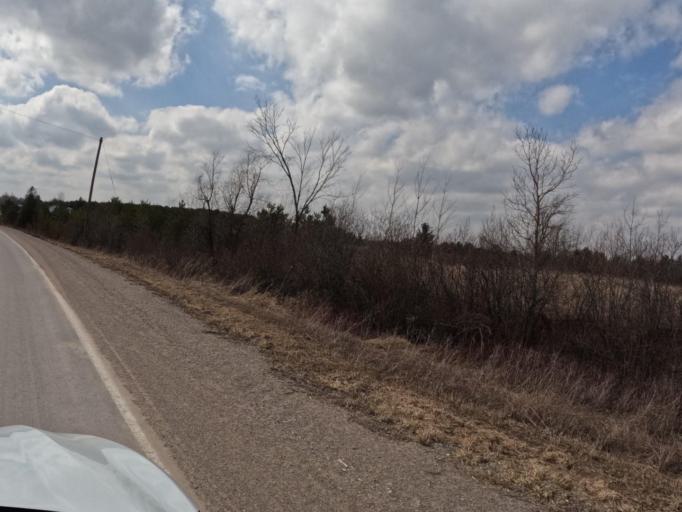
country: CA
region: Ontario
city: Shelburne
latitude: 44.0058
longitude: -80.2282
